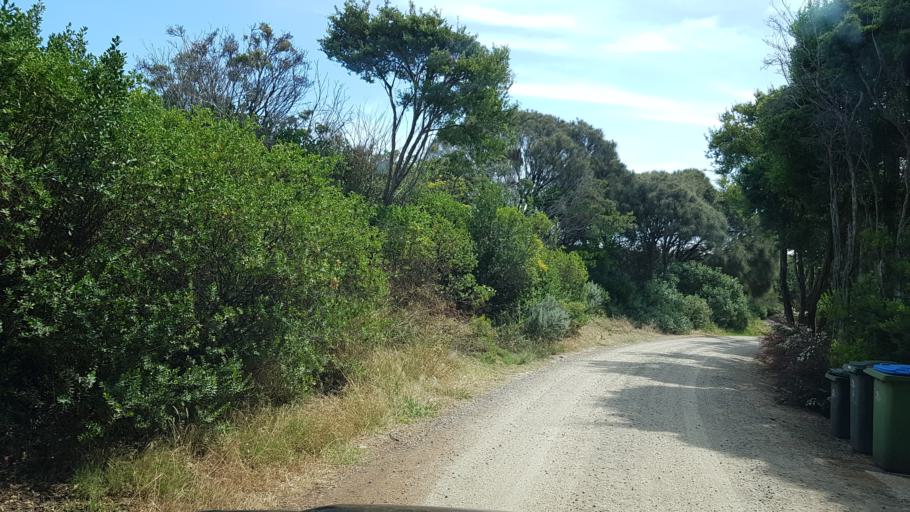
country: AU
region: Victoria
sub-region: Mornington Peninsula
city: Sorrento
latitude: -38.3203
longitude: 144.7073
